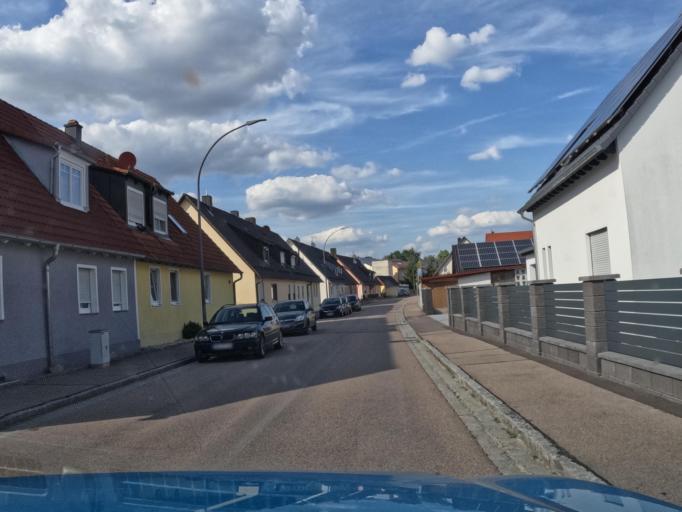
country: DE
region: Bavaria
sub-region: Upper Palatinate
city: Schwarzenfeld
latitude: 49.3858
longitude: 12.1233
